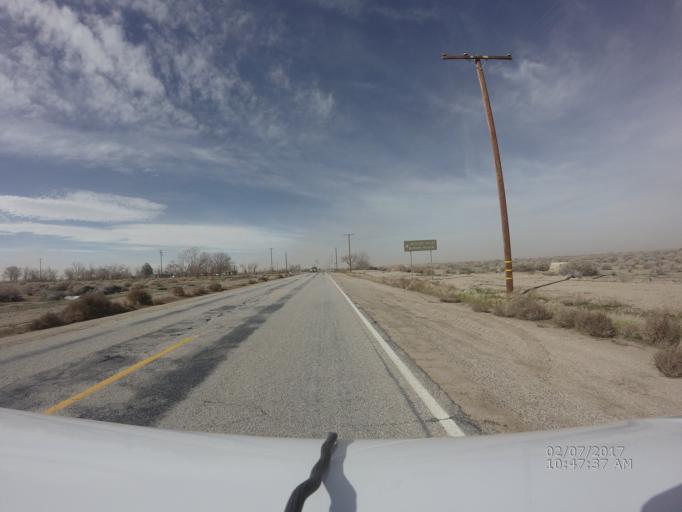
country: US
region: California
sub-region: Los Angeles County
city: Lake Los Angeles
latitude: 34.6901
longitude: -117.8616
